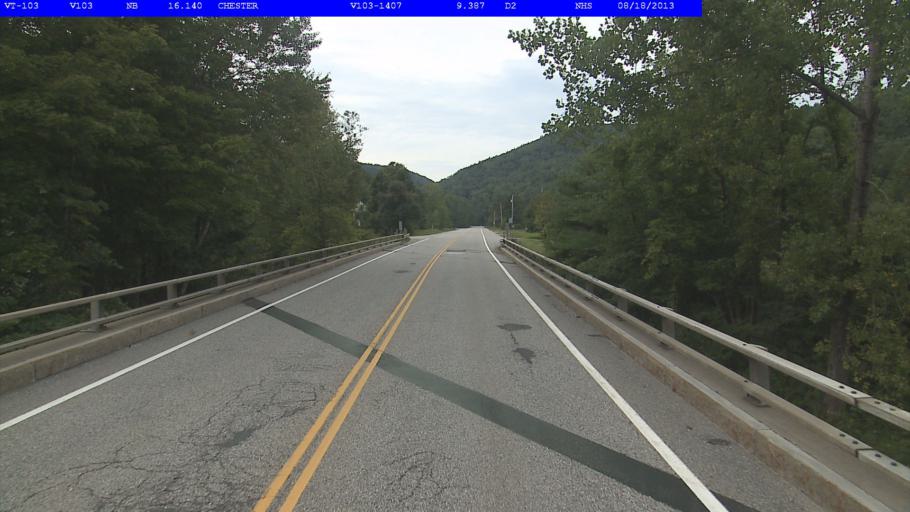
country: US
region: Vermont
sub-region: Windsor County
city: Chester
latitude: 43.3448
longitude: -72.6229
